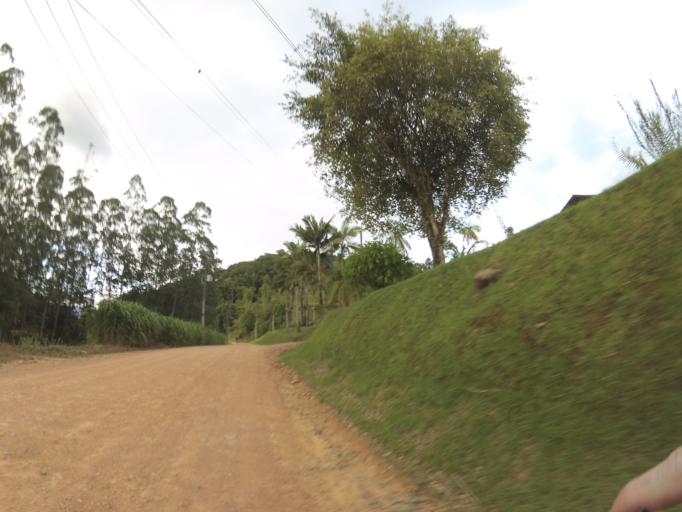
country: BR
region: Santa Catarina
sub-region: Pomerode
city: Pomerode
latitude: -26.7633
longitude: -49.1646
